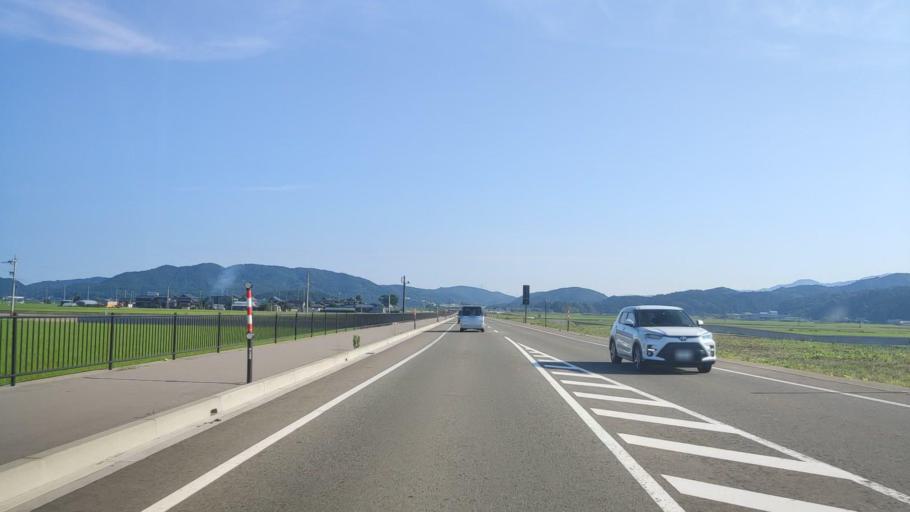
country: JP
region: Fukui
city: Maruoka
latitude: 36.1825
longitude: 136.2679
